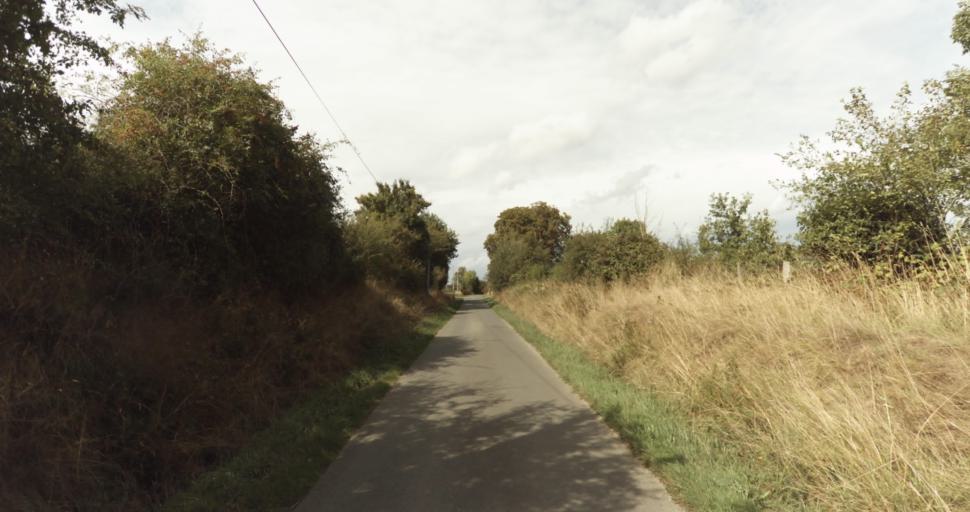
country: FR
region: Lower Normandy
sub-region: Departement du Calvados
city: Orbec
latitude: 48.9141
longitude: 0.3818
